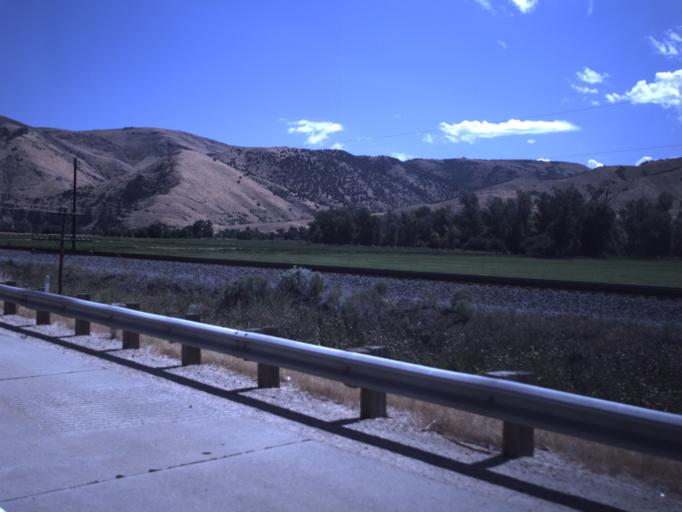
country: US
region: Utah
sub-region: Morgan County
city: Morgan
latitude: 41.0494
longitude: -111.6349
